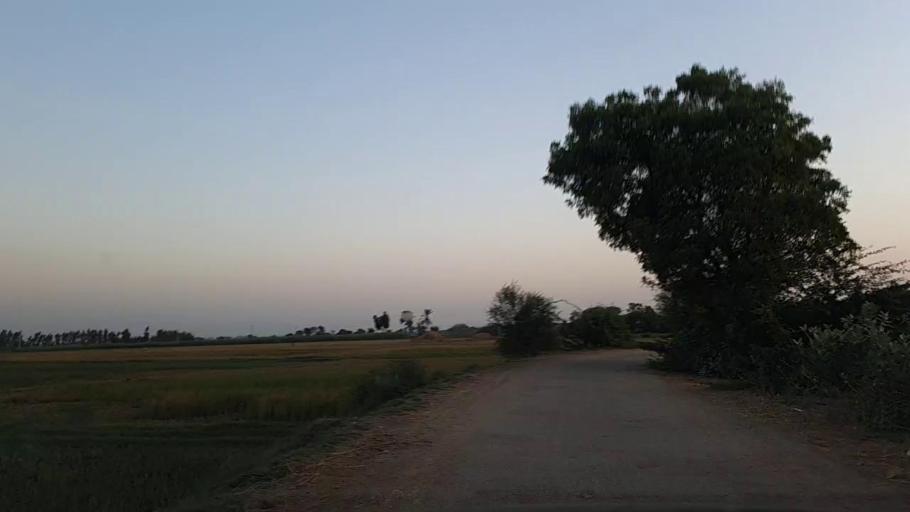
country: PK
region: Sindh
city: Mirpur Batoro
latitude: 24.6154
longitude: 68.1847
